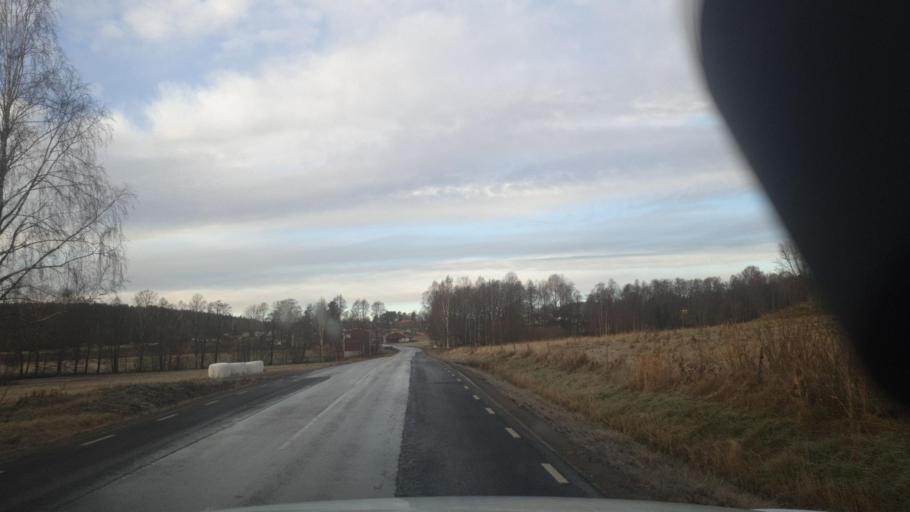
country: SE
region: Vaermland
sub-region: Arvika Kommun
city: Arvika
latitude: 59.7906
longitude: 12.6189
